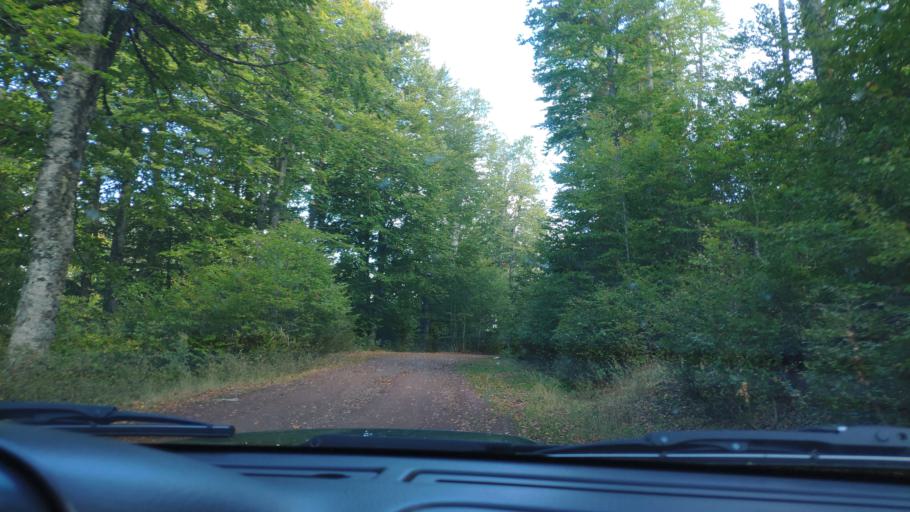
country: GR
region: West Macedonia
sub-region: Nomos Kastorias
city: Nestorio
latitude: 40.3145
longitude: 20.9115
